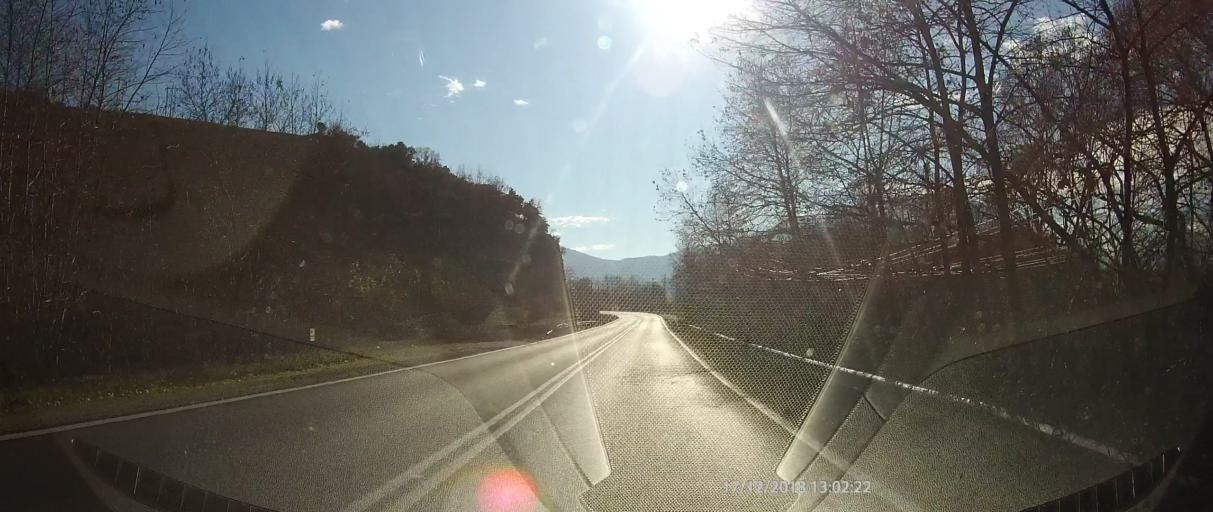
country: GR
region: Thessaly
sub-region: Trikala
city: Kastraki
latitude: 39.7247
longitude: 21.5939
